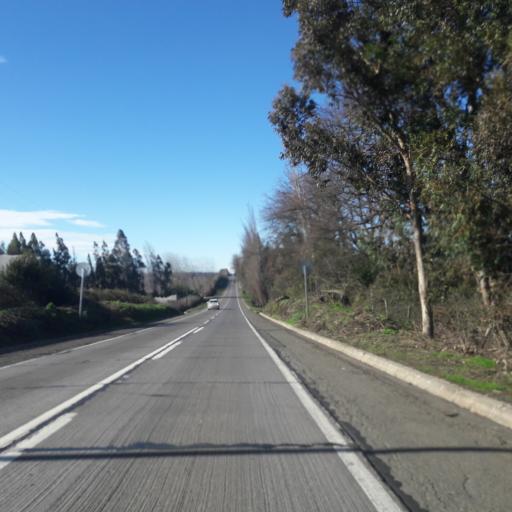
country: CL
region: Araucania
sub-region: Provincia de Malleco
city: Angol
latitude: -37.7496
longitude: -72.5901
